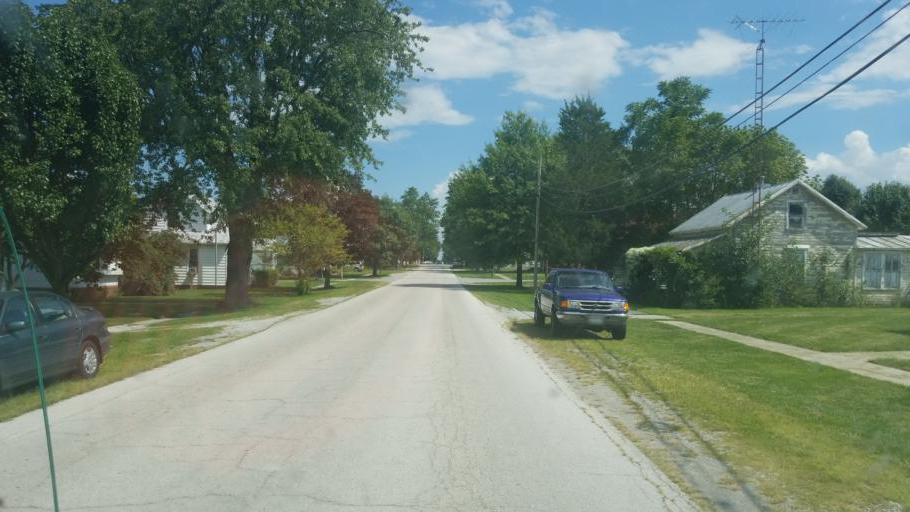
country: US
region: Ohio
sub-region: Hardin County
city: Forest
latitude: 40.8614
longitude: -83.4663
